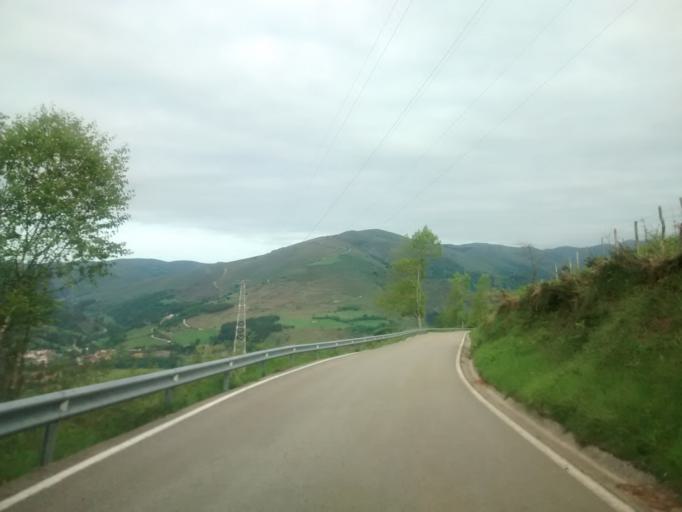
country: ES
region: Cantabria
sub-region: Provincia de Cantabria
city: San Vicente de la Barquera
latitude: 43.2529
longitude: -4.4311
